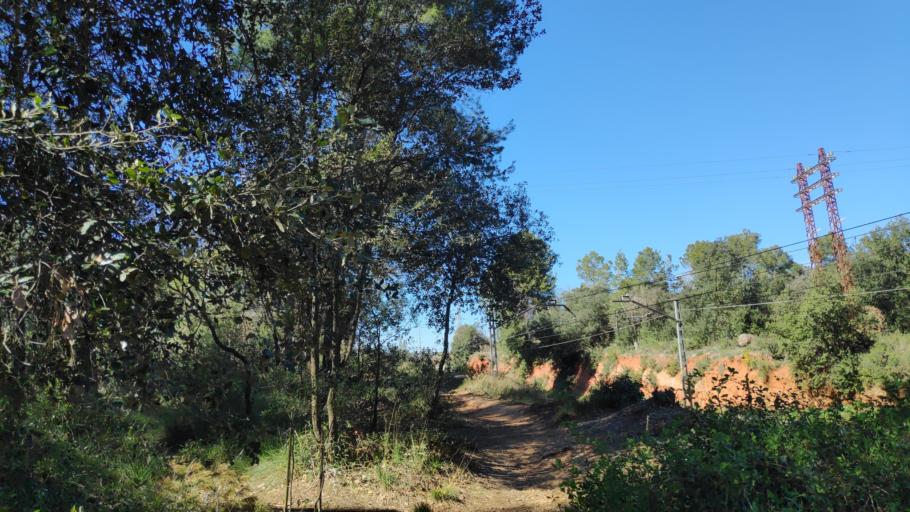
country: ES
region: Catalonia
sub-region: Provincia de Barcelona
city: Sant Quirze del Valles
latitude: 41.5648
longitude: 2.0653
